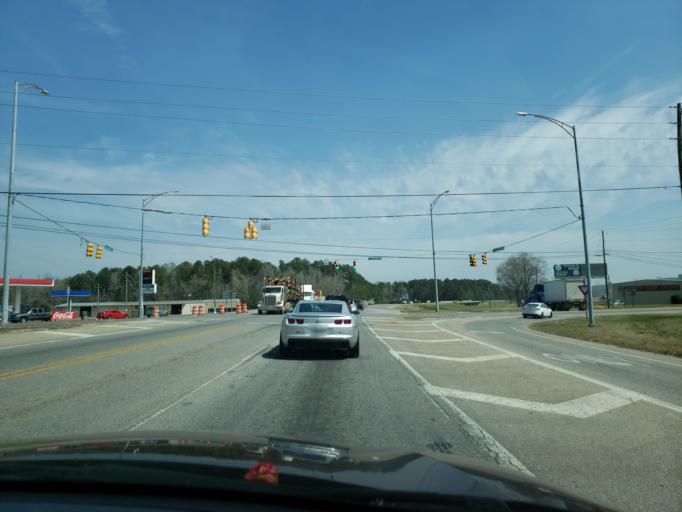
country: US
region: Alabama
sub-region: Elmore County
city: Wetumpka
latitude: 32.5535
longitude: -86.2160
